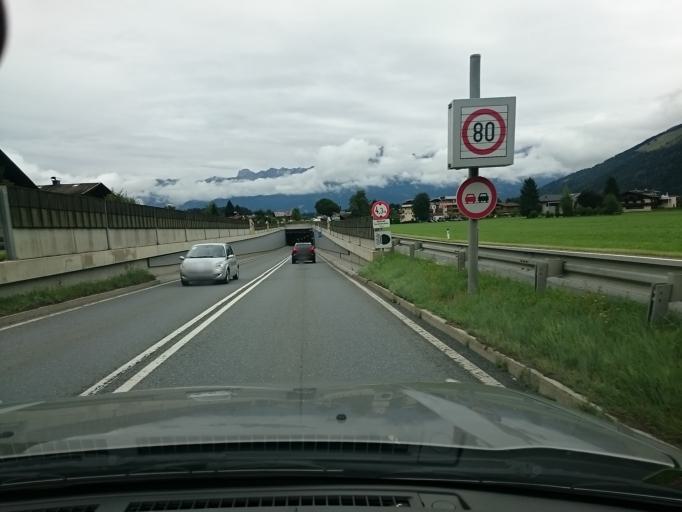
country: AT
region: Salzburg
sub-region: Politischer Bezirk Zell am See
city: Maishofen
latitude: 47.3654
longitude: 12.8024
